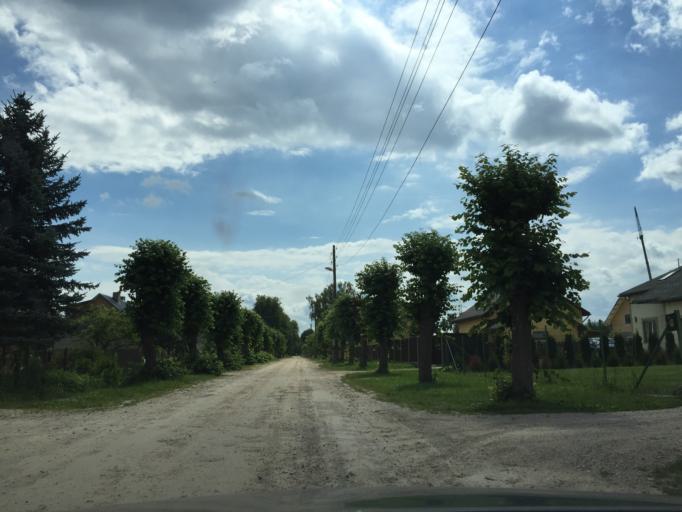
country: LV
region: Jelgava
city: Jelgava
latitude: 56.6502
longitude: 23.6799
